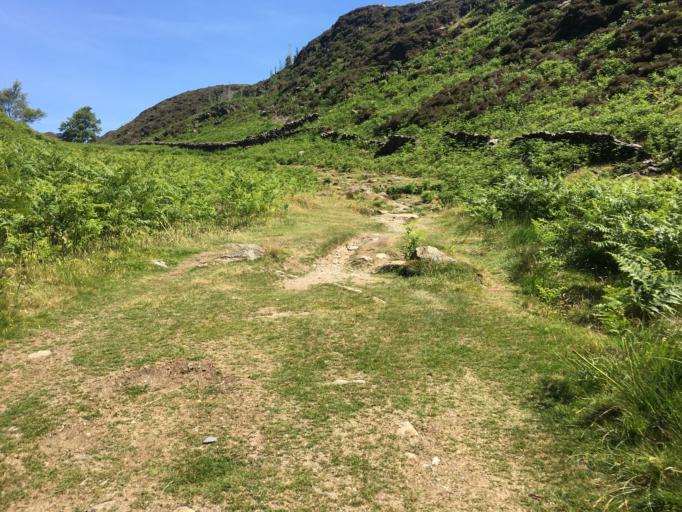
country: GB
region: Wales
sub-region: Gwynedd
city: Penrhyndeudraeth
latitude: 53.0028
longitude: -4.0848
